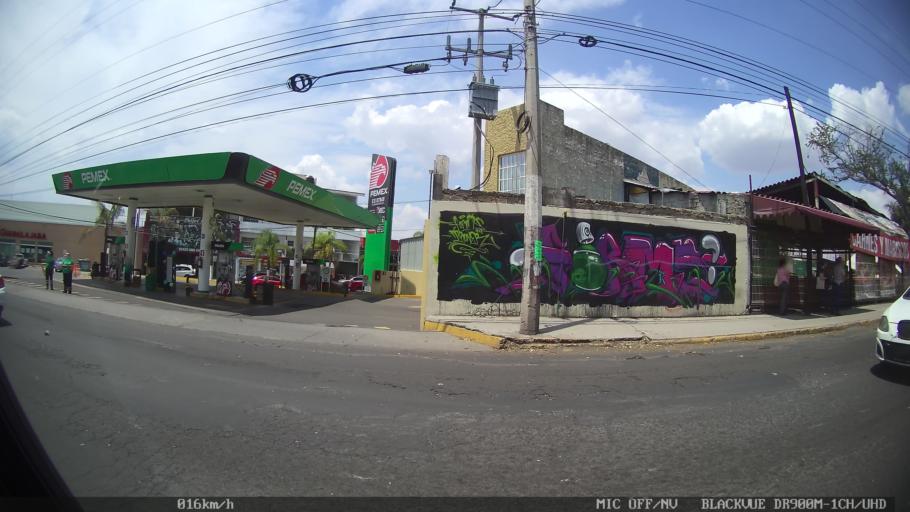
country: MX
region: Jalisco
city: Tlaquepaque
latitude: 20.6358
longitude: -103.2734
